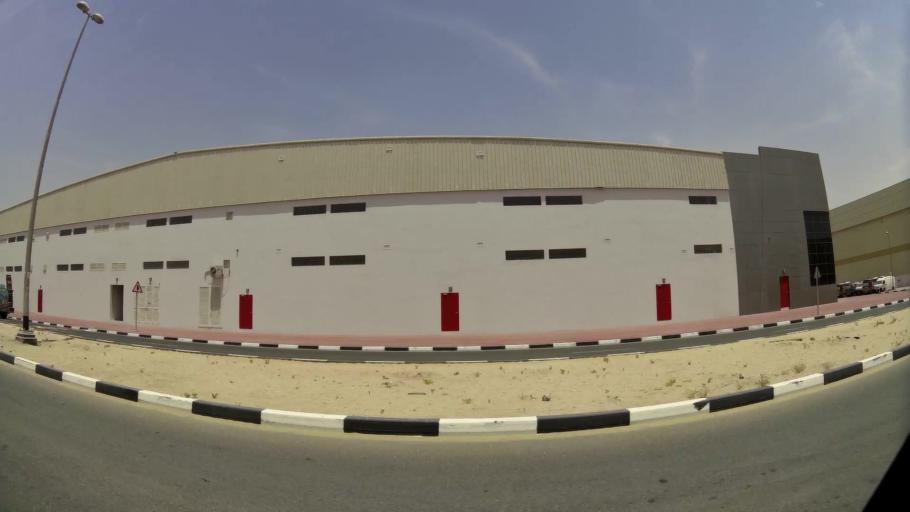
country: AE
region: Ash Shariqah
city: Sharjah
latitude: 25.1881
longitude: 55.3815
